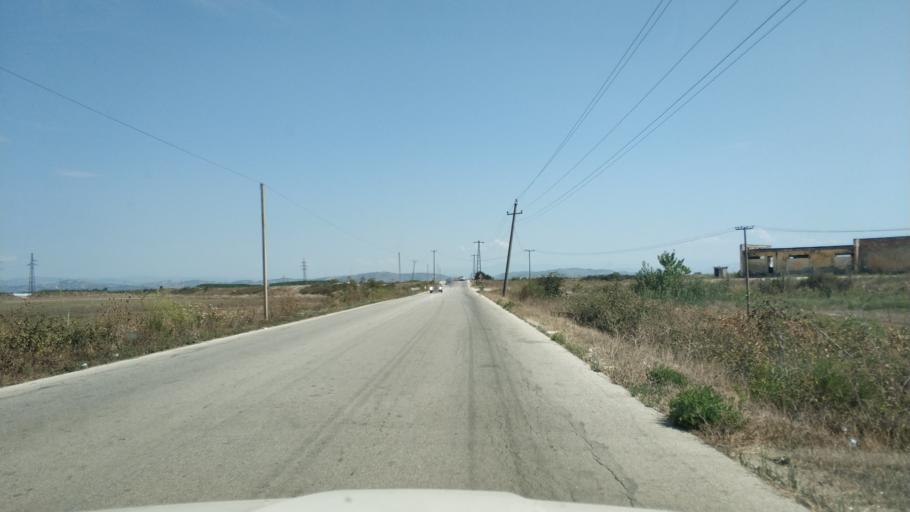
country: AL
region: Fier
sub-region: Rrethi i Lushnjes
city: Gradishte
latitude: 40.8855
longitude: 19.5927
